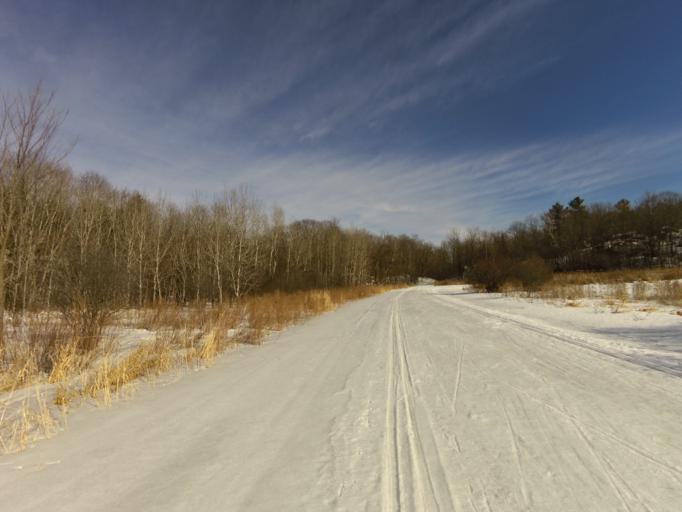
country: CA
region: Quebec
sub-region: Outaouais
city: Gatineau
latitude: 45.4656
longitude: -75.7848
